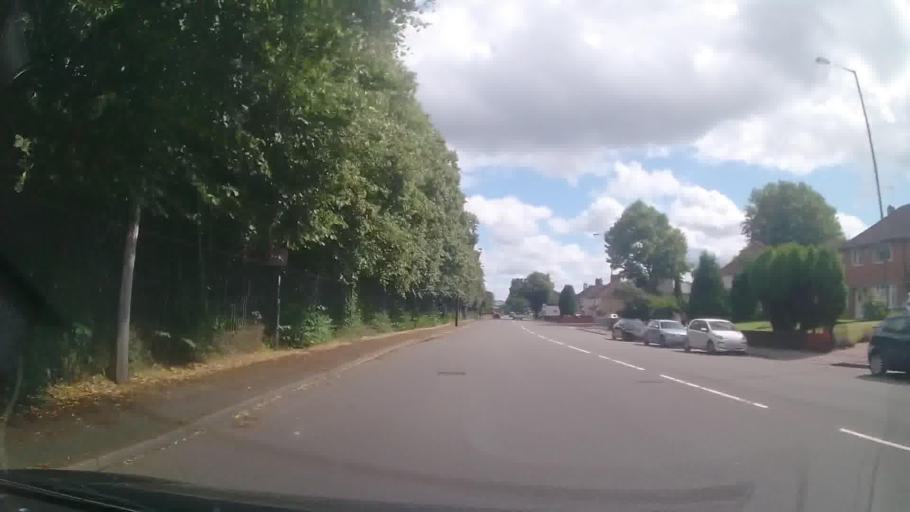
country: GB
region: England
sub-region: Walsall
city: Darlaston
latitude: 52.5697
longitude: -2.0177
